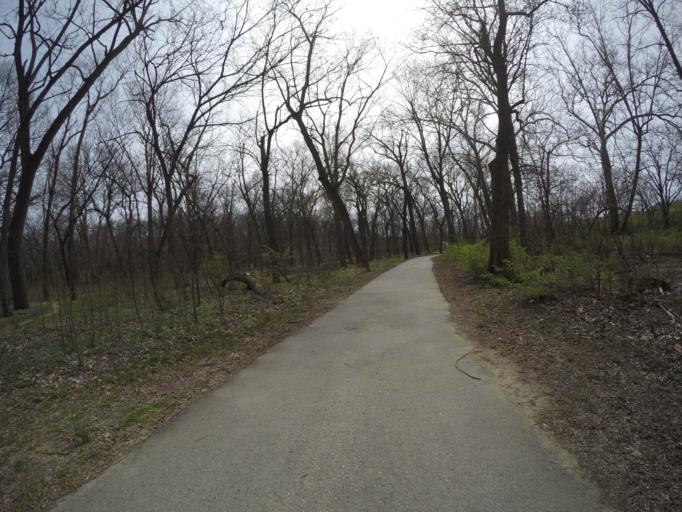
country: US
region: Kansas
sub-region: Johnson County
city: Leawood
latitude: 38.9301
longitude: -94.6209
